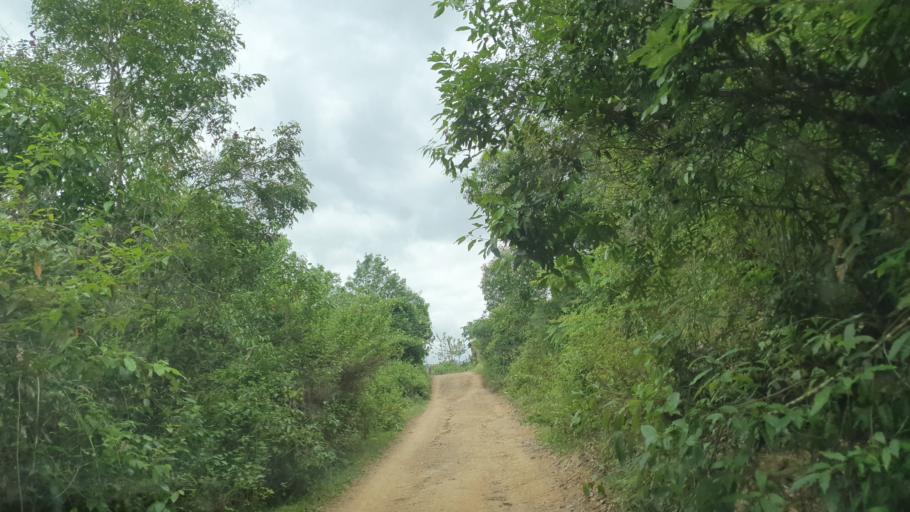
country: VN
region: Nghe An
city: Muong Xen
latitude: 19.3269
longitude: 103.7319
